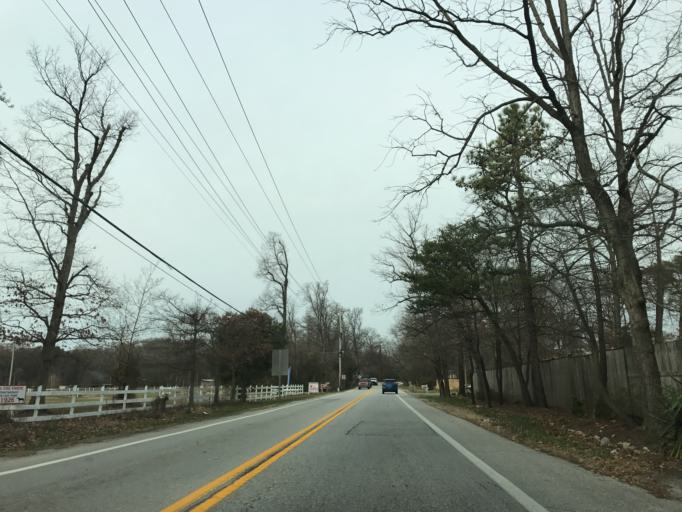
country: US
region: Maryland
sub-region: Anne Arundel County
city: Pasadena
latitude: 39.1038
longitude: -76.5525
